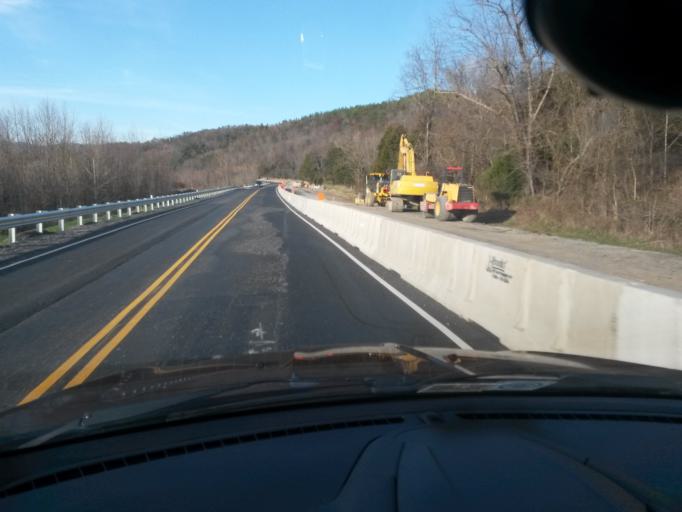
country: US
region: Virginia
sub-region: Alleghany County
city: Clifton Forge
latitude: 37.6677
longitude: -79.7959
